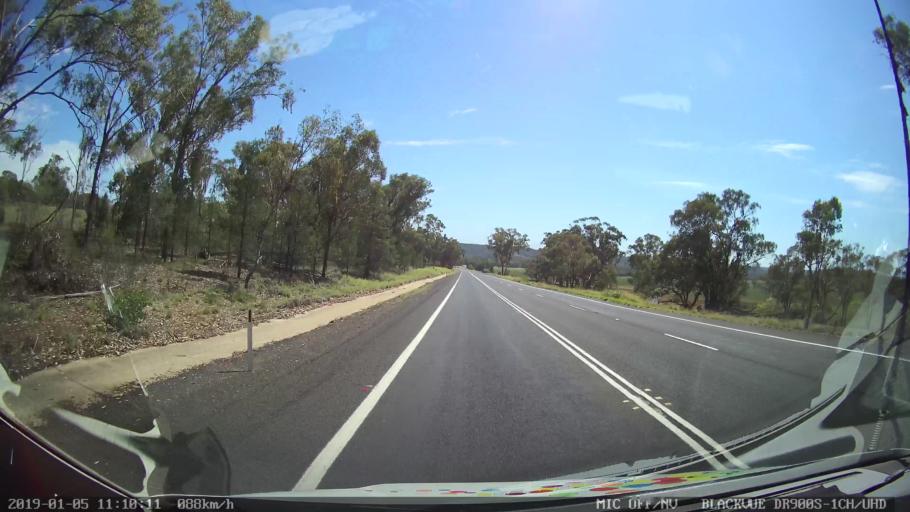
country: AU
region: New South Wales
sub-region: Warrumbungle Shire
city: Coonabarabran
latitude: -31.4091
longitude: 149.2418
